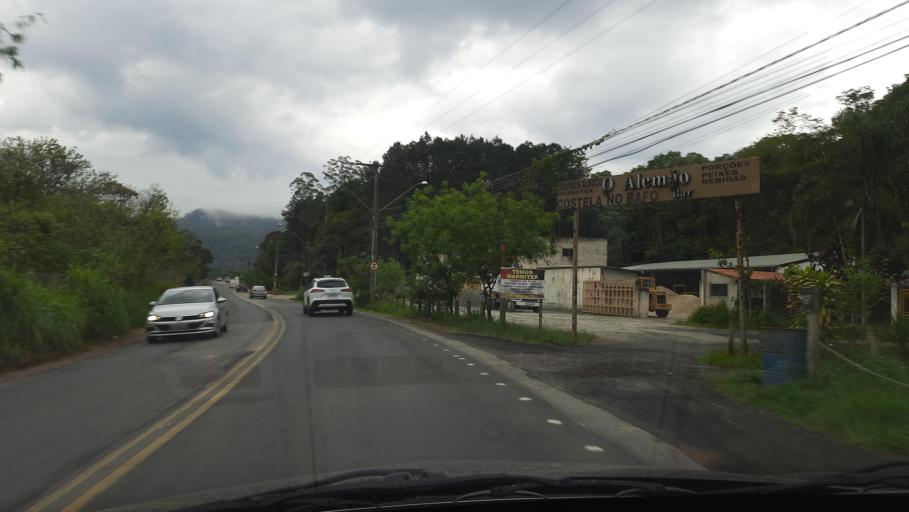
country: BR
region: Sao Paulo
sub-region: Franco Da Rocha
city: Franco da Rocha
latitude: -23.3449
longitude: -46.6617
